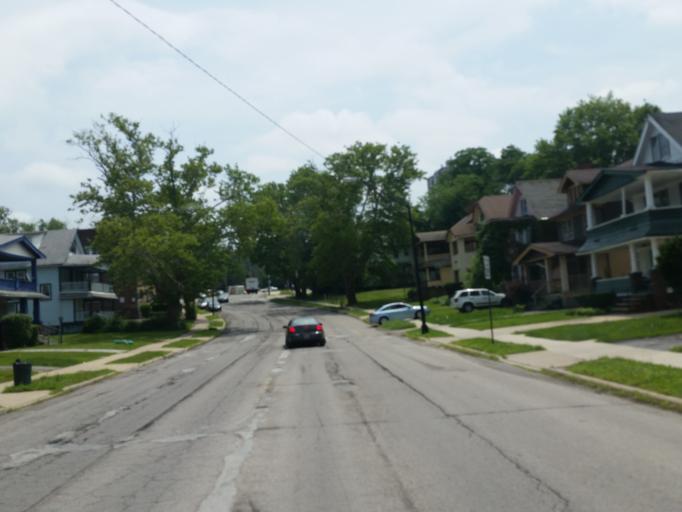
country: US
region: Ohio
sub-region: Cuyahoga County
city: East Cleveland
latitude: 41.5445
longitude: -81.5700
